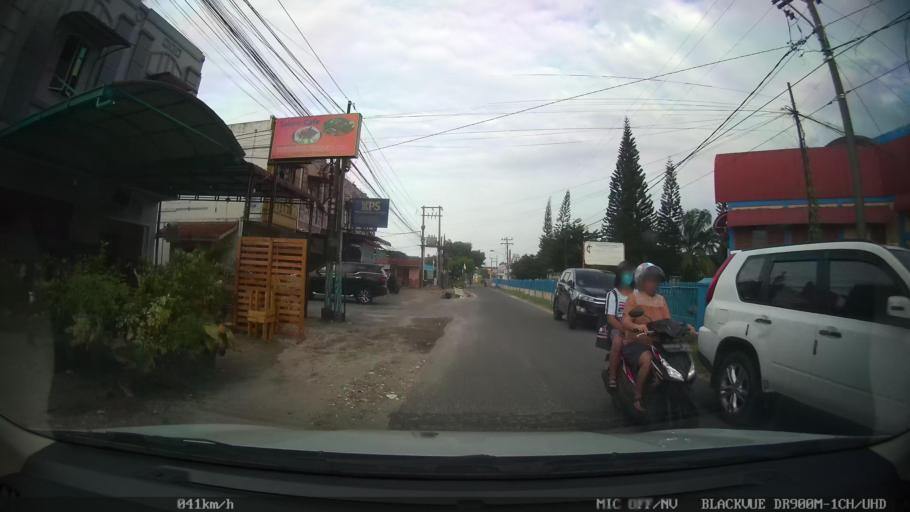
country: ID
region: North Sumatra
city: Sunggal
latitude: 3.5550
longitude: 98.6295
